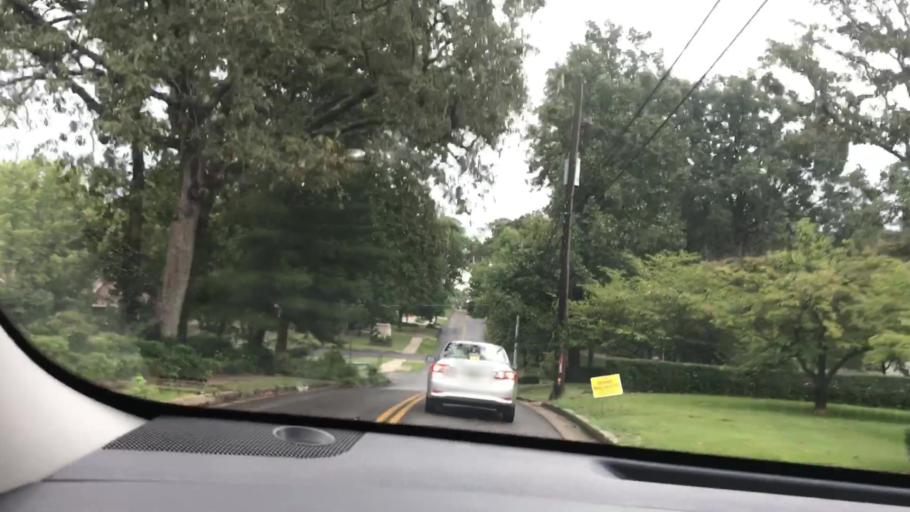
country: US
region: Kentucky
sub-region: Calloway County
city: Murray
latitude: 36.6030
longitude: -88.3226
